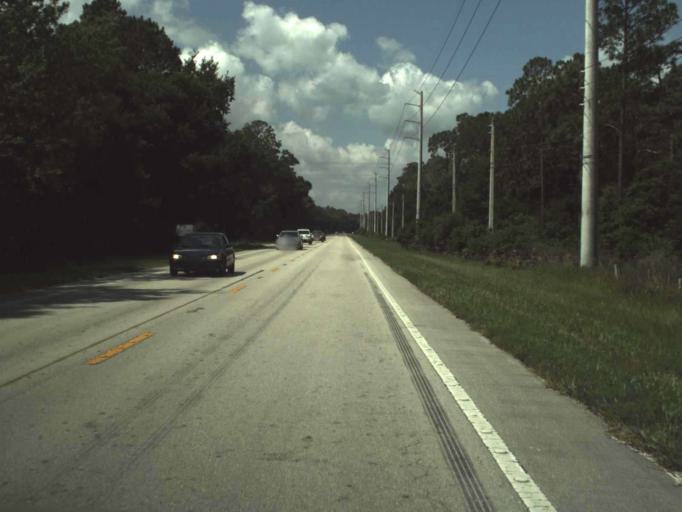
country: US
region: Florida
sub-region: Volusia County
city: Deltona
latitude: 28.8916
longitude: -81.1405
